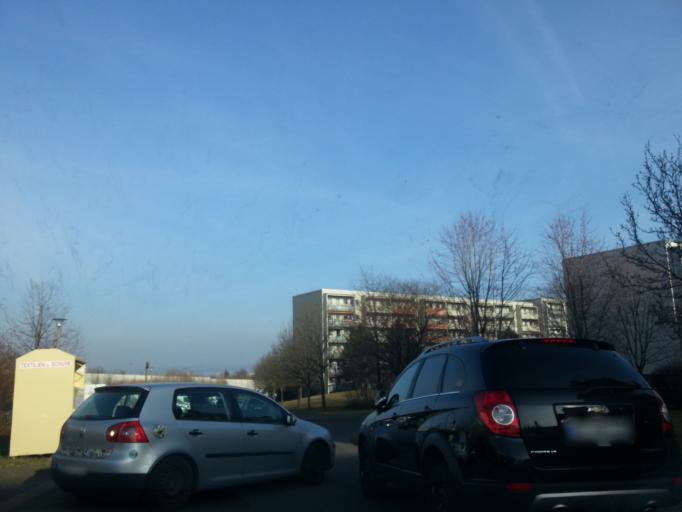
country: DE
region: Saxony
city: Freital
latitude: 51.0487
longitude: 13.6640
